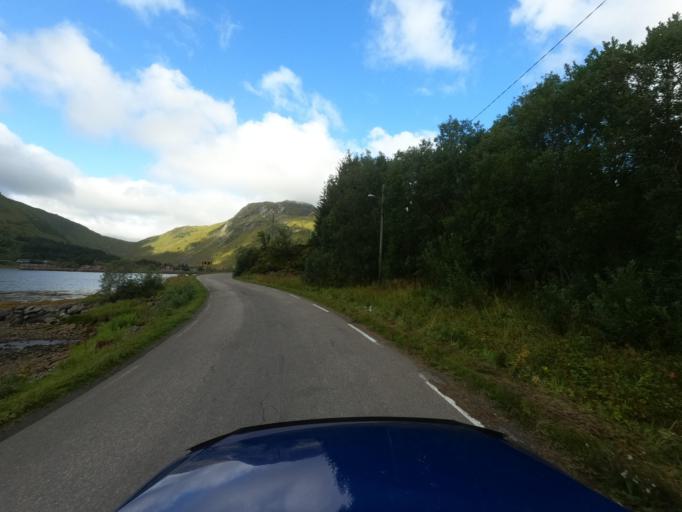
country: NO
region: Nordland
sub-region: Vestvagoy
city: Evjen
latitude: 68.2019
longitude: 13.8983
